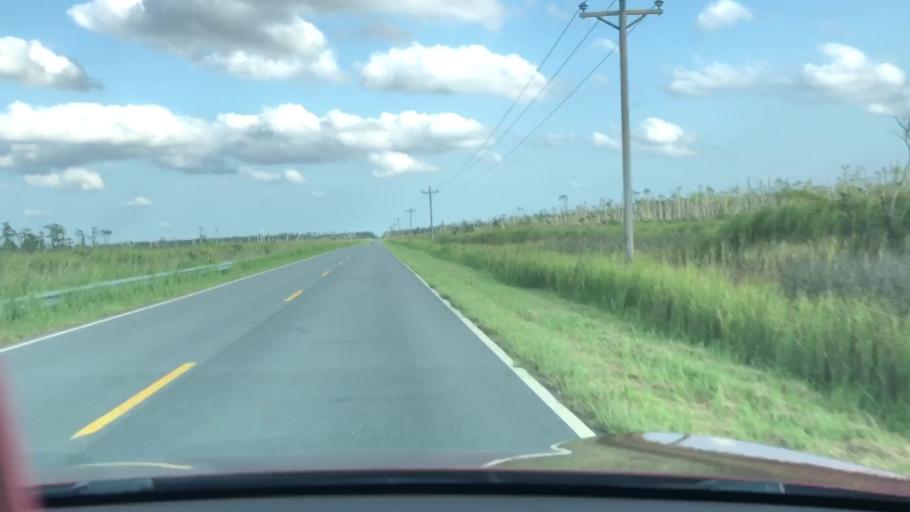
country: US
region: North Carolina
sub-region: Dare County
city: Wanchese
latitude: 35.6300
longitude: -75.8527
